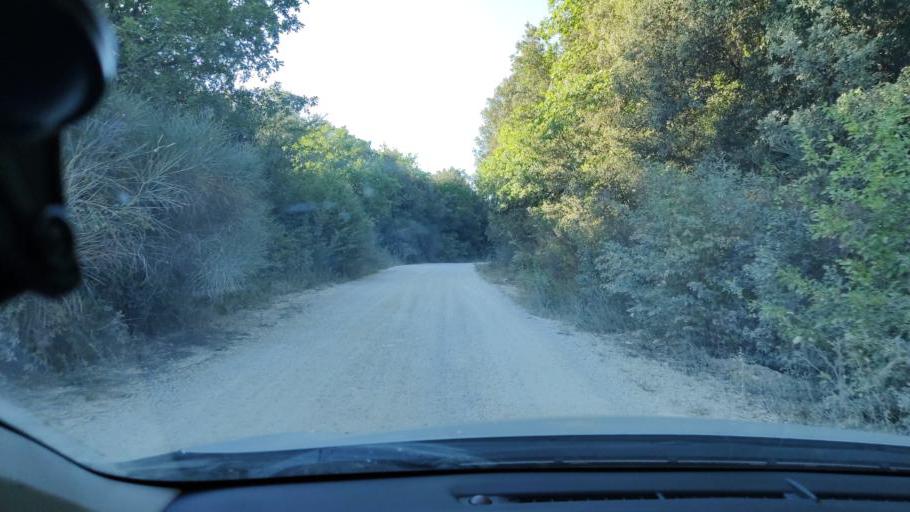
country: IT
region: Umbria
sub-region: Provincia di Terni
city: Amelia
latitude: 42.5354
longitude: 12.3794
